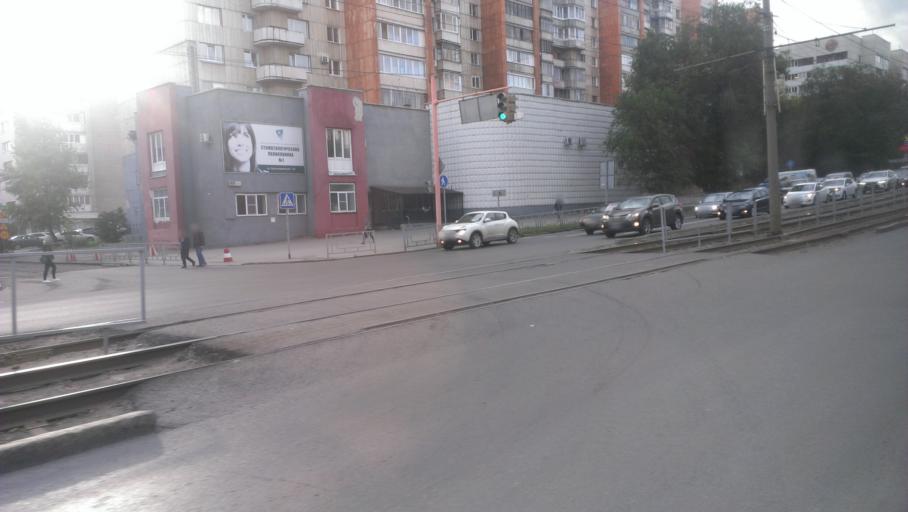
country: RU
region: Altai Krai
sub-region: Gorod Barnaulskiy
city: Barnaul
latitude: 53.3429
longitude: 83.7688
